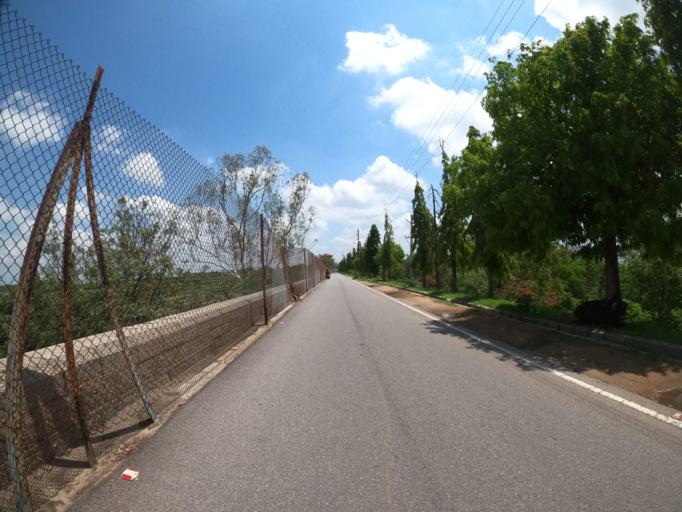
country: IN
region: Telangana
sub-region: Medak
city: Serilingampalle
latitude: 17.3835
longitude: 78.3168
